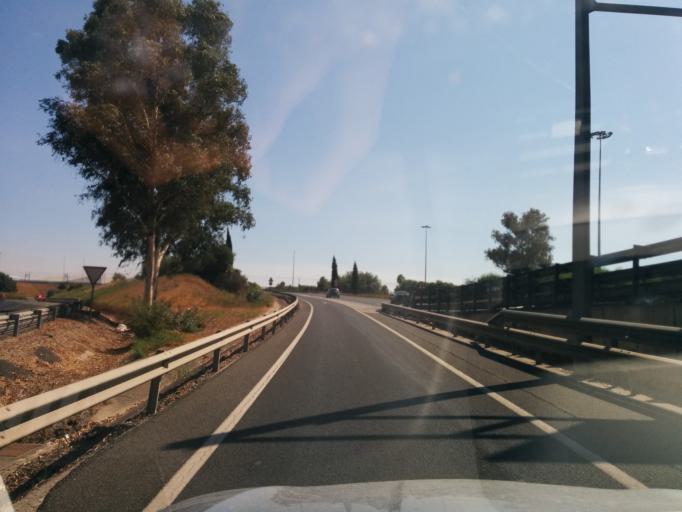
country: ES
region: Andalusia
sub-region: Provincia de Sevilla
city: San Juan de Aznalfarache
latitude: 37.3711
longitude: -6.0156
